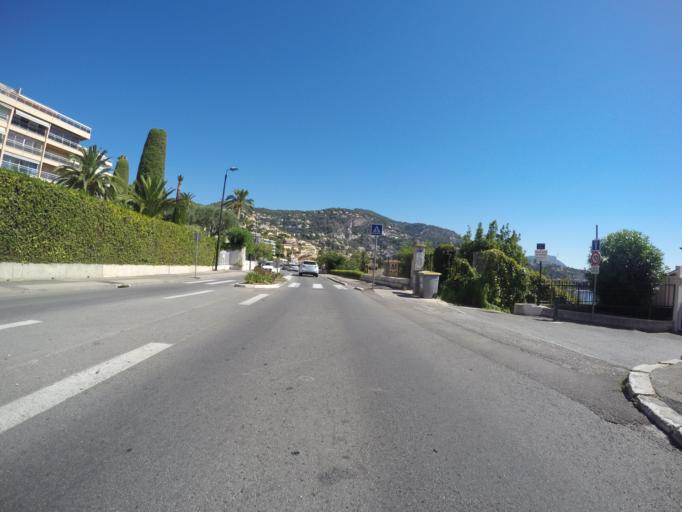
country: FR
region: Provence-Alpes-Cote d'Azur
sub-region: Departement des Alpes-Maritimes
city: Villefranche-sur-Mer
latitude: 43.6988
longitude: 7.3051
